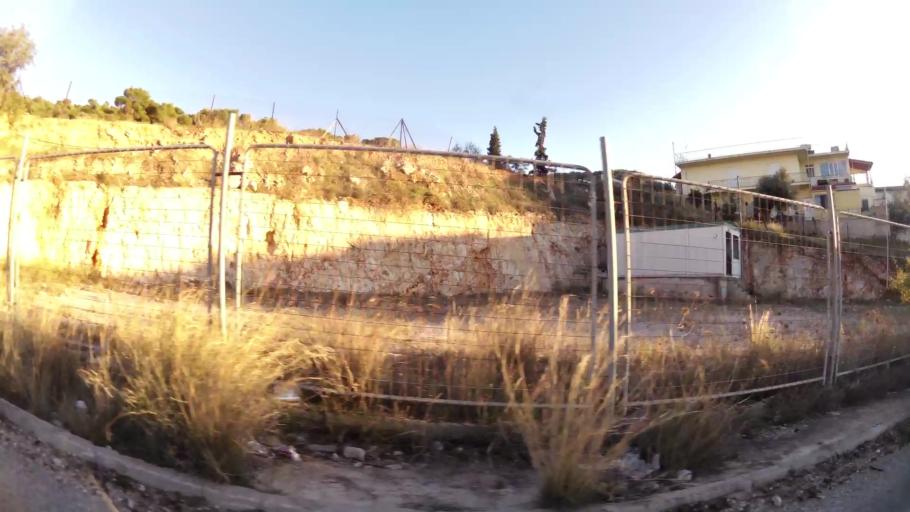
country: GR
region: Attica
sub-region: Nomarchia Athinas
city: Chaidari
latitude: 38.0361
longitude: 23.6374
